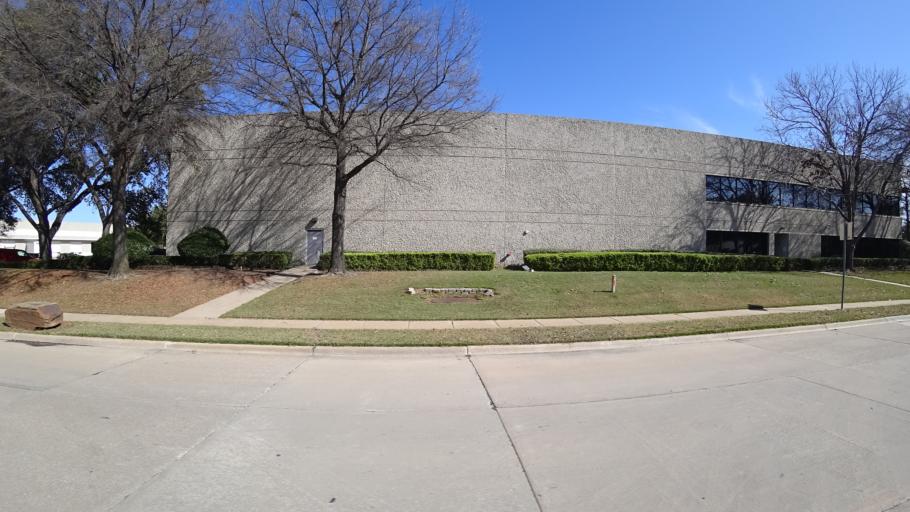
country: US
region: Texas
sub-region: Denton County
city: Lewisville
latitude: 33.0218
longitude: -96.9785
